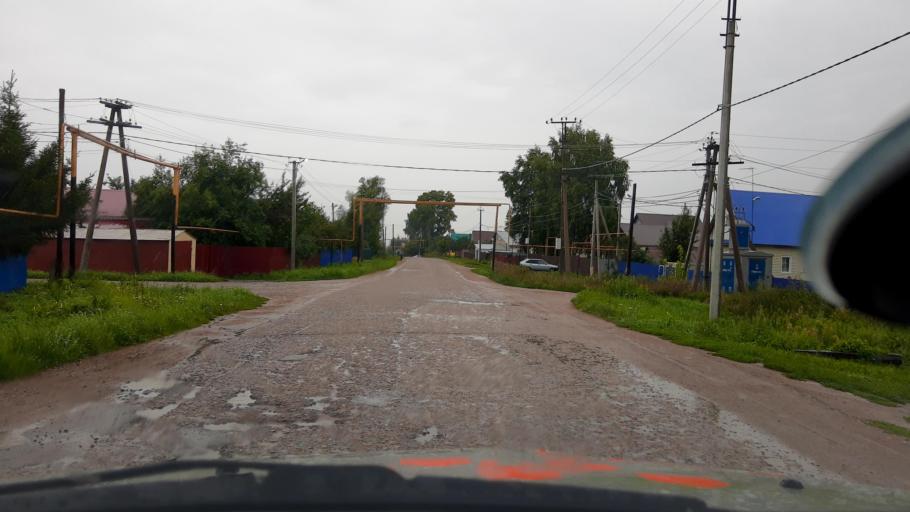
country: RU
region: Bashkortostan
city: Iglino
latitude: 54.8103
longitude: 56.3937
